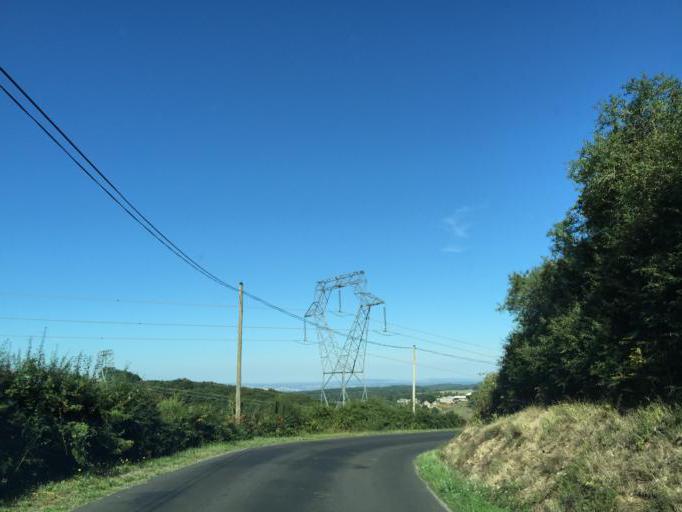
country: FR
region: Midi-Pyrenees
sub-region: Departement de l'Aveyron
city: Laissac
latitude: 44.3425
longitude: 2.7726
